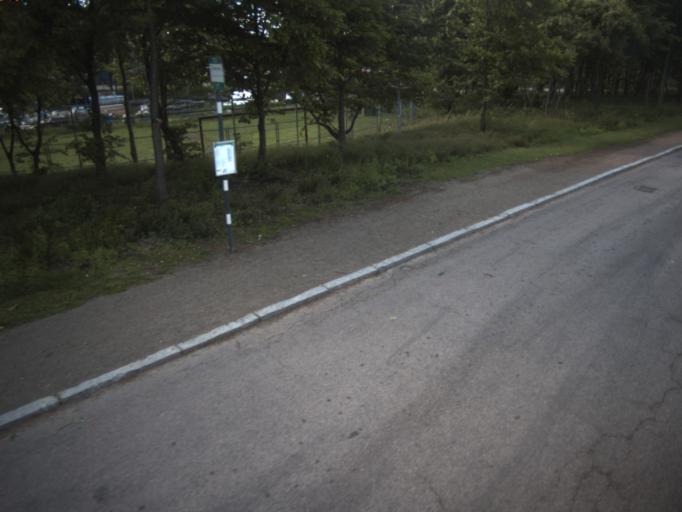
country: SE
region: Skane
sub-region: Helsingborg
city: Helsingborg
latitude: 56.0353
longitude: 12.7189
